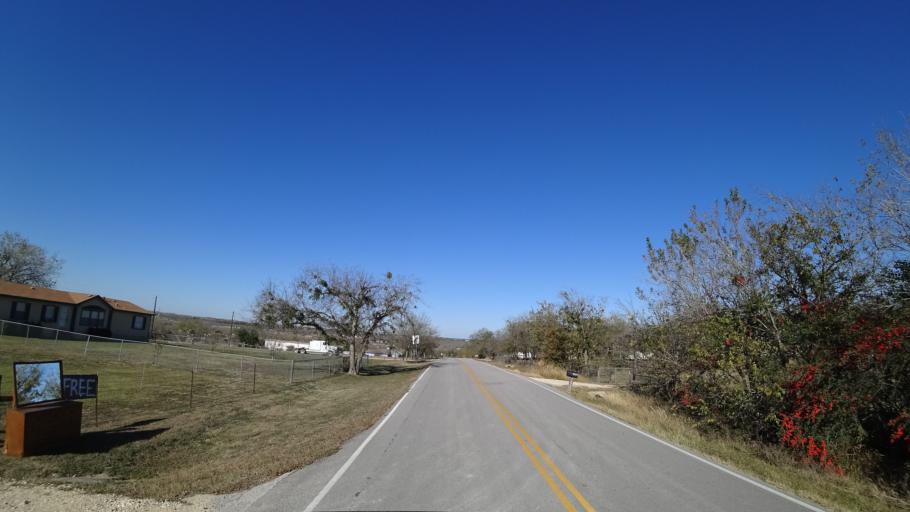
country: US
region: Texas
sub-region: Travis County
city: Onion Creek
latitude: 30.1050
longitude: -97.6720
